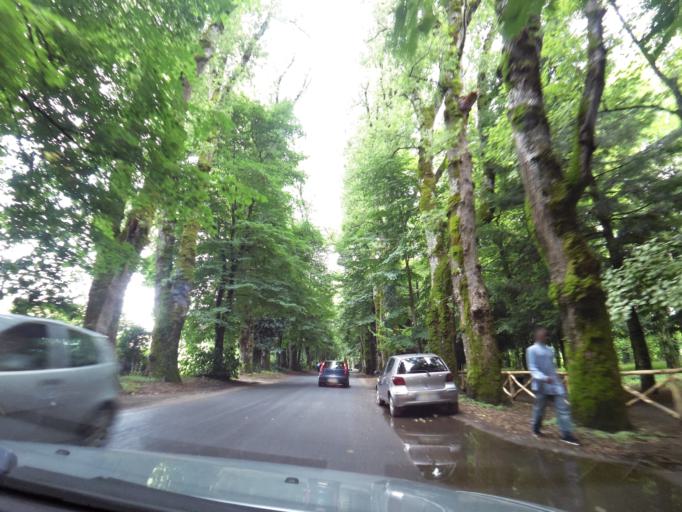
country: IT
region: Calabria
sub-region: Provincia di Vibo-Valentia
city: Serra San Bruno
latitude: 38.5702
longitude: 16.3239
